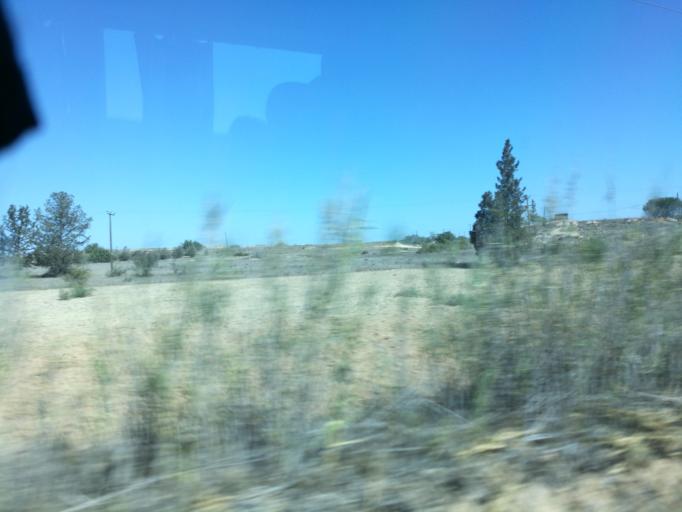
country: CY
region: Ammochostos
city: Acheritou
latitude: 35.0781
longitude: 33.8674
